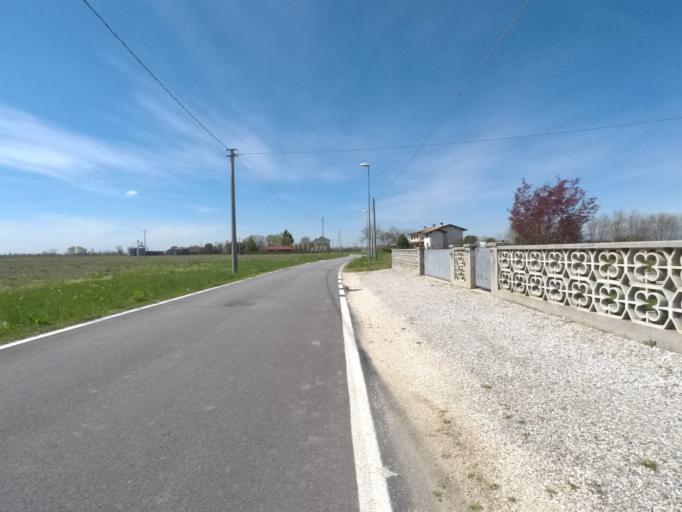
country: IT
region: Friuli Venezia Giulia
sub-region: Provincia di Udine
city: Camino al Tagliamento
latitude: 45.9522
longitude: 12.9245
